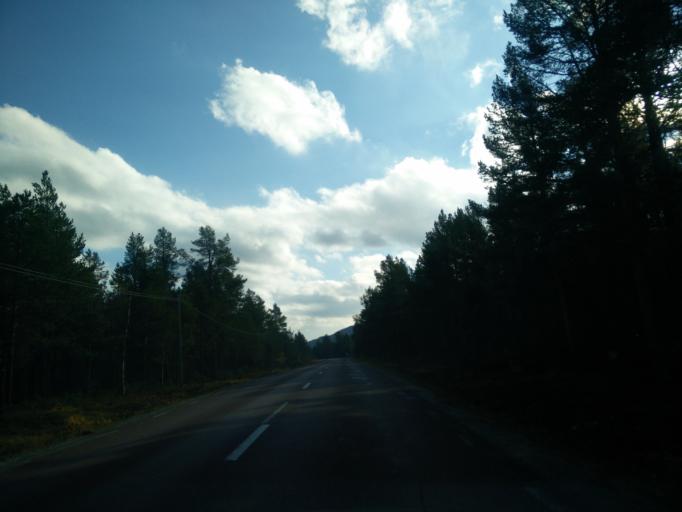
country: NO
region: Hedmark
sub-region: Engerdal
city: Engerdal
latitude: 62.4954
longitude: 12.6343
